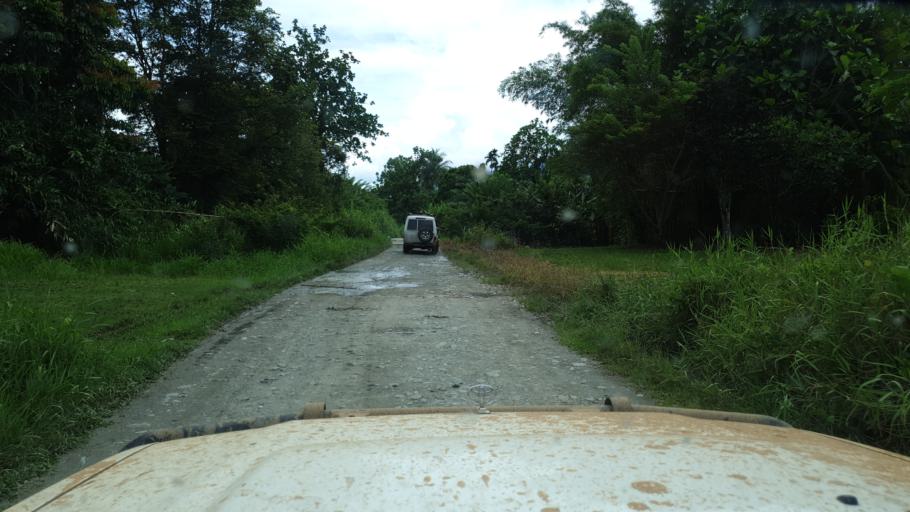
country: PG
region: Northern Province
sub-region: Sohe
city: Kokoda
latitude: -8.9181
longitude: 147.8637
